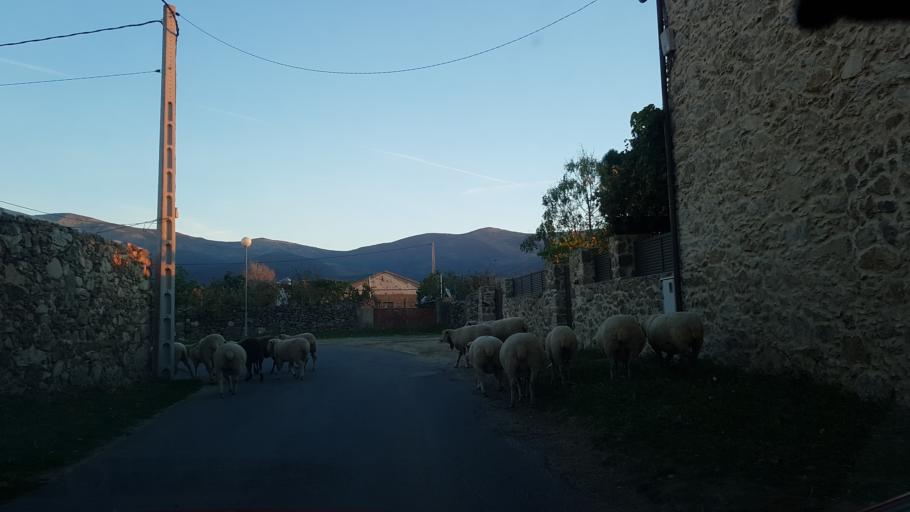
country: ES
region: Castille and Leon
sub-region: Provincia de Segovia
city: Ortigosa del Monte
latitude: 40.8515
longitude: -4.1634
